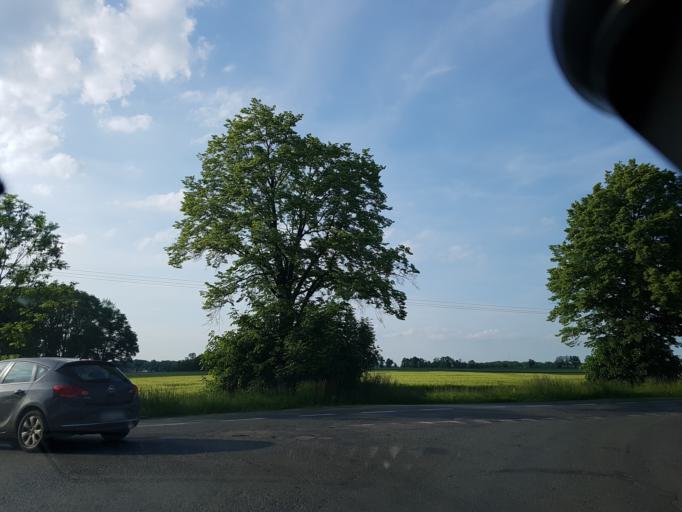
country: PL
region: Lower Silesian Voivodeship
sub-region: Powiat wroclawski
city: Zorawina
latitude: 50.9171
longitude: 17.0033
